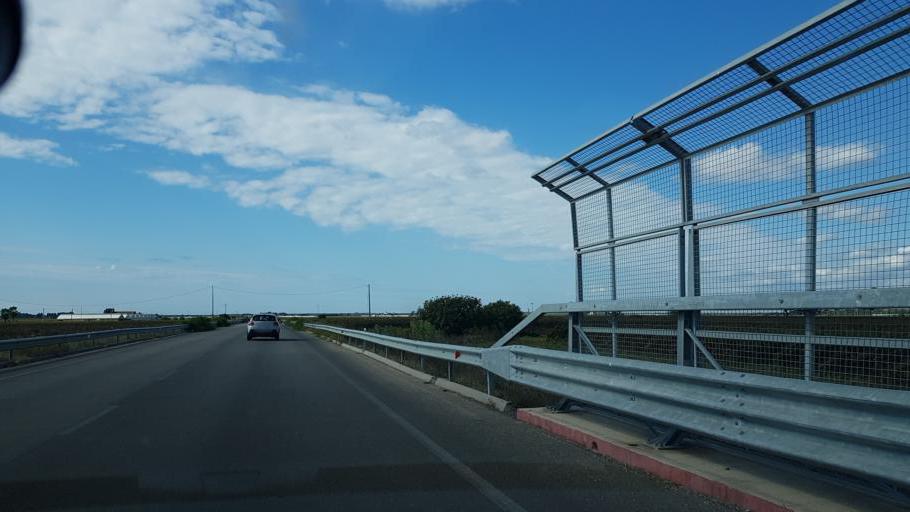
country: IT
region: Apulia
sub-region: Provincia di Lecce
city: Leverano
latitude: 40.3051
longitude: 17.9876
